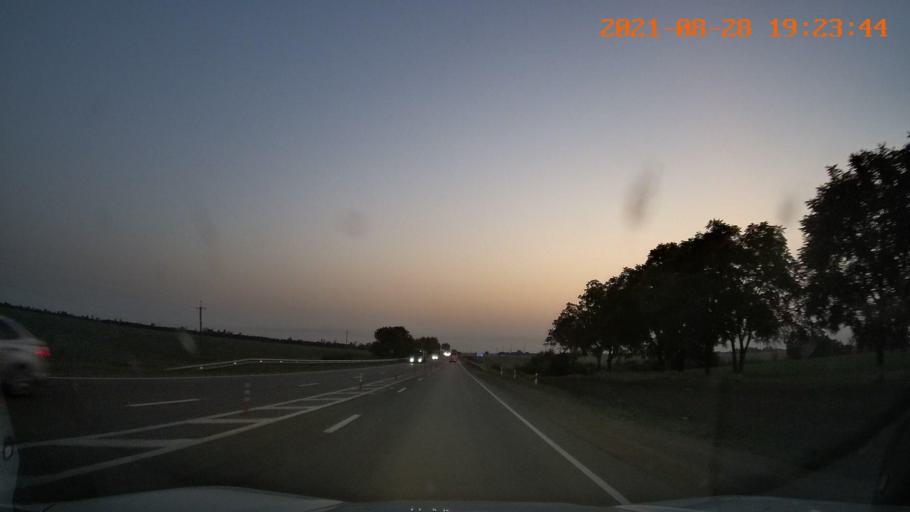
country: RU
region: Adygeya
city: Ponezhukay
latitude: 44.8740
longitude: 39.4453
